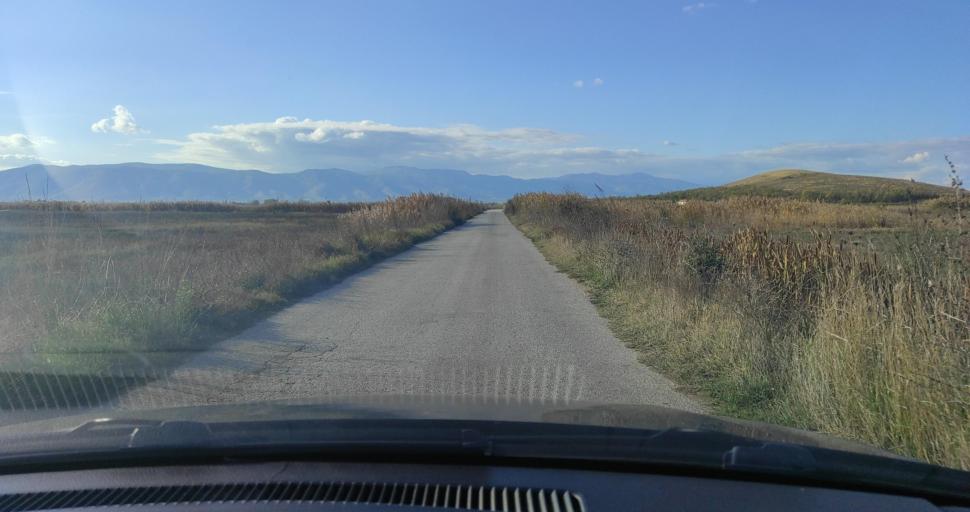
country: MK
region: Prilep
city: Topolcani
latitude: 41.2803
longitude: 21.4254
